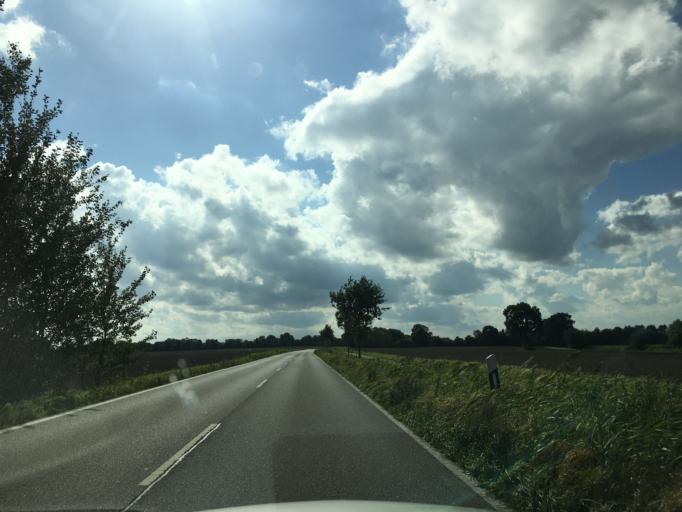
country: DE
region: Schleswig-Holstein
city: Krokau
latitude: 54.4073
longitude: 10.3694
